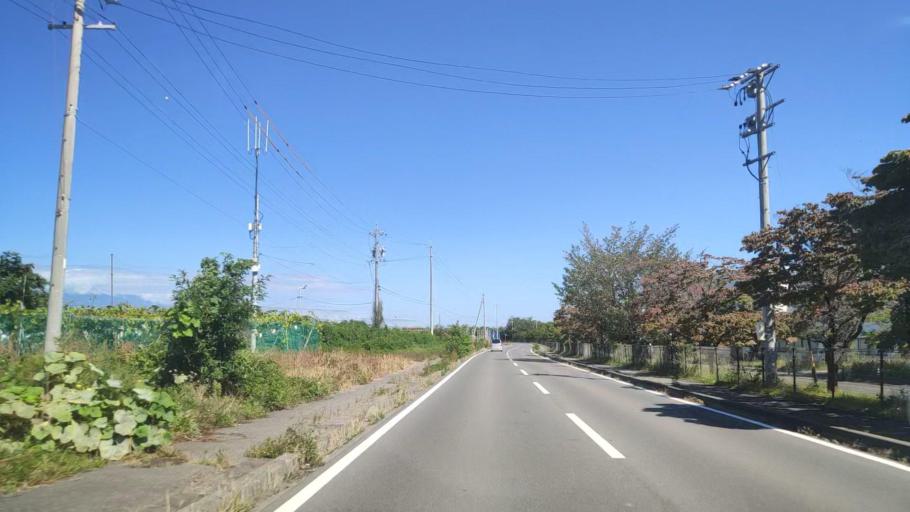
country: JP
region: Nagano
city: Shiojiri
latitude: 36.1647
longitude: 137.9176
